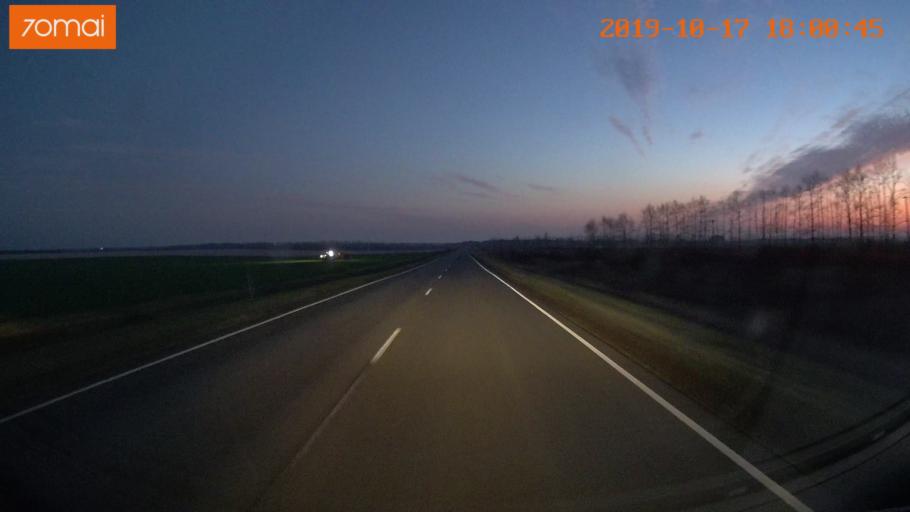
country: RU
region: Tula
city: Kurkino
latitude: 53.5171
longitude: 38.6134
